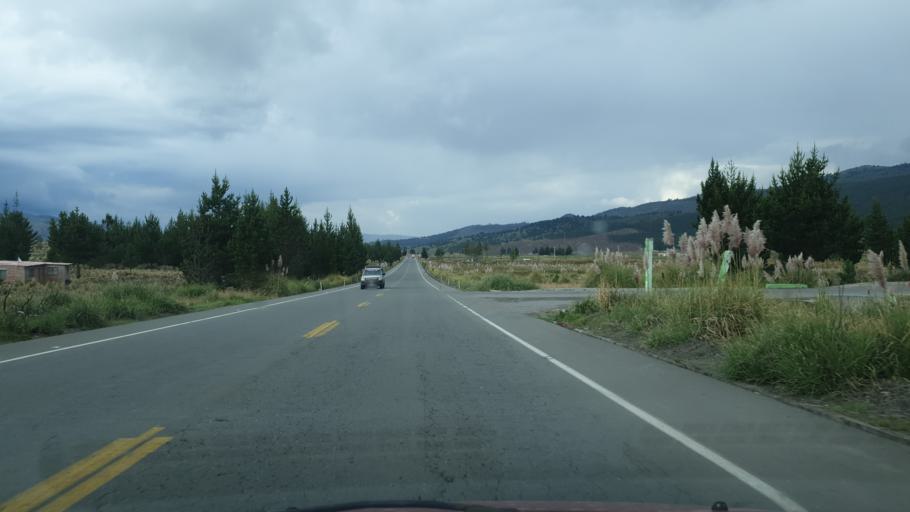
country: EC
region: Chimborazo
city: Alausi
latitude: -2.0247
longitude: -78.7333
